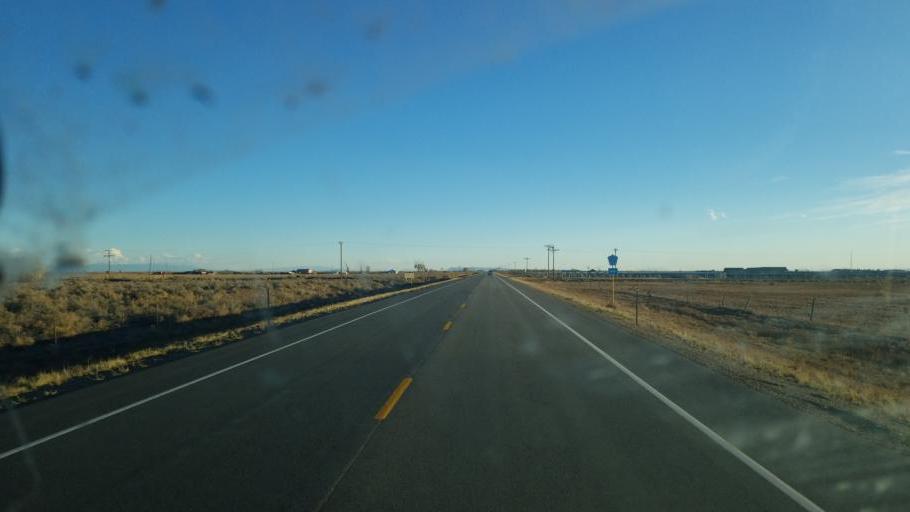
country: US
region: Colorado
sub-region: Alamosa County
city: Alamosa East
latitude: 37.6934
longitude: -105.8747
